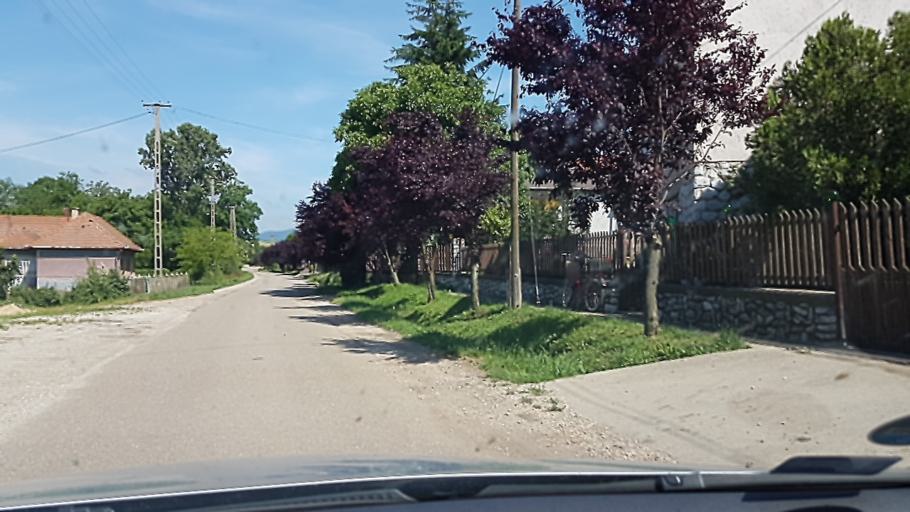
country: HU
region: Borsod-Abauj-Zemplen
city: Saly
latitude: 47.9517
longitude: 20.6980
